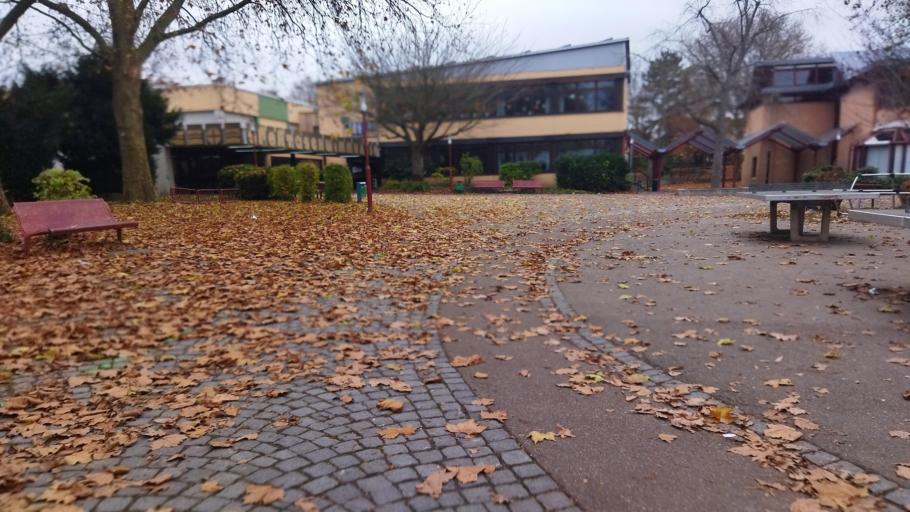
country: DE
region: Baden-Wuerttemberg
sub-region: Regierungsbezirk Stuttgart
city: Leingarten
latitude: 49.1436
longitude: 9.1108
